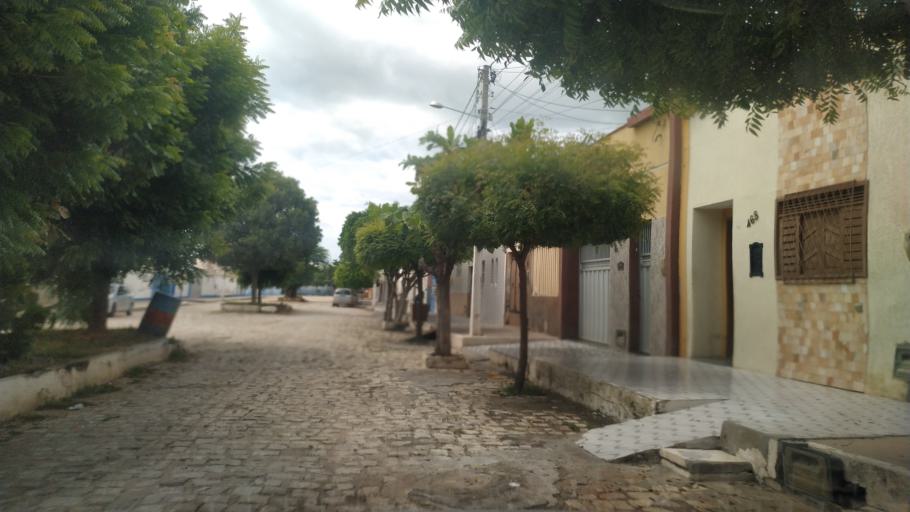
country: BR
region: Rio Grande do Norte
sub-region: Areia Branca
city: Areia Branca
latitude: -4.9527
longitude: -37.1356
